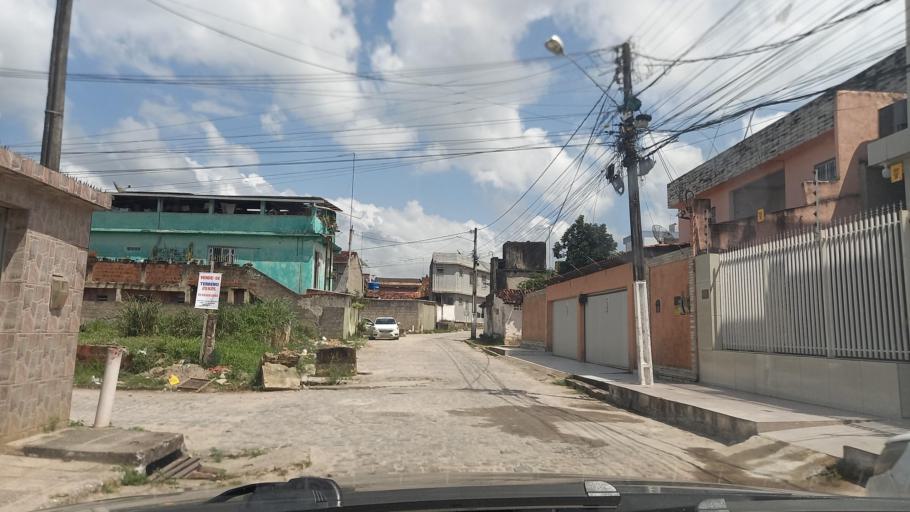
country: BR
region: Pernambuco
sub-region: Goiana
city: Goiana
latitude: -7.5650
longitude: -34.9992
